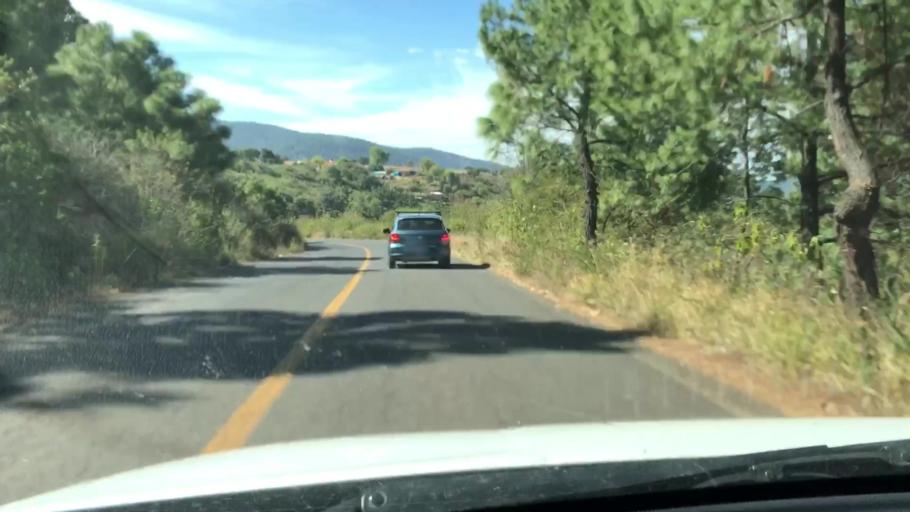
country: MX
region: Jalisco
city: Chiquilistlan
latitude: 20.1411
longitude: -103.7177
